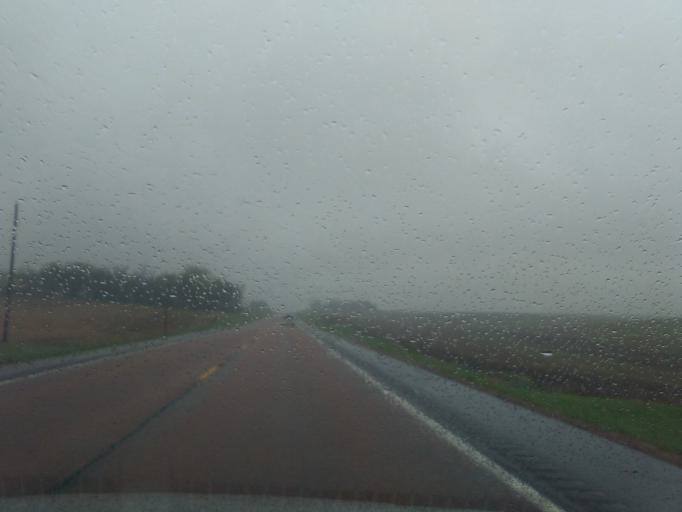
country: US
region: Nebraska
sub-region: Wayne County
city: Wayne
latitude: 42.2355
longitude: -97.1457
